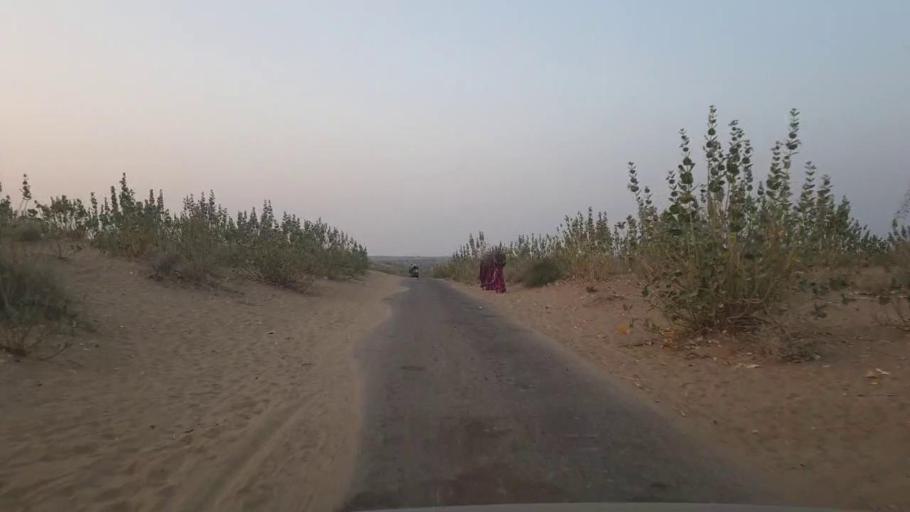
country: PK
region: Sindh
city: Umarkot
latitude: 25.2943
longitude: 70.0764
